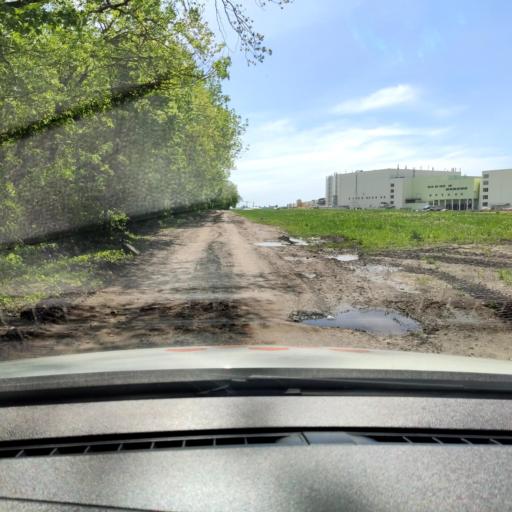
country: RU
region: Voronezj
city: Podgornoye
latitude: 51.7907
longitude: 39.2104
